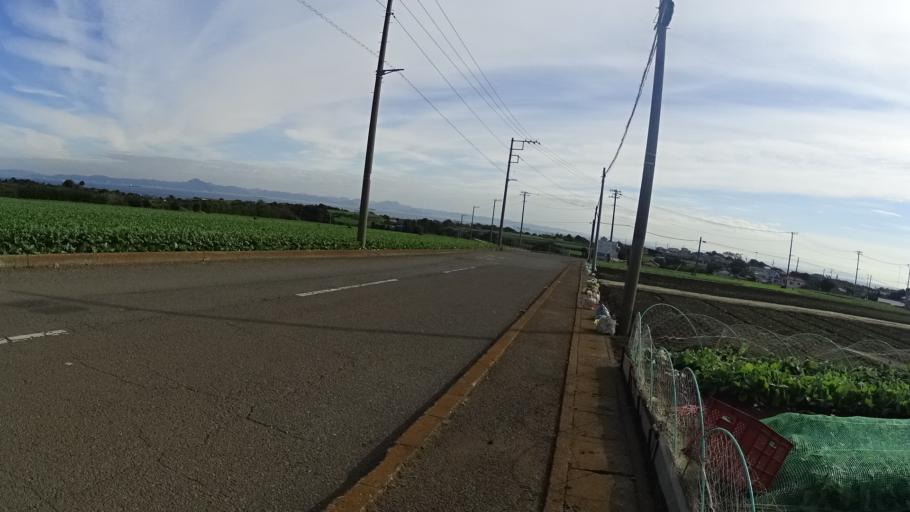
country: JP
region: Kanagawa
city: Miura
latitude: 35.1526
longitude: 139.6708
